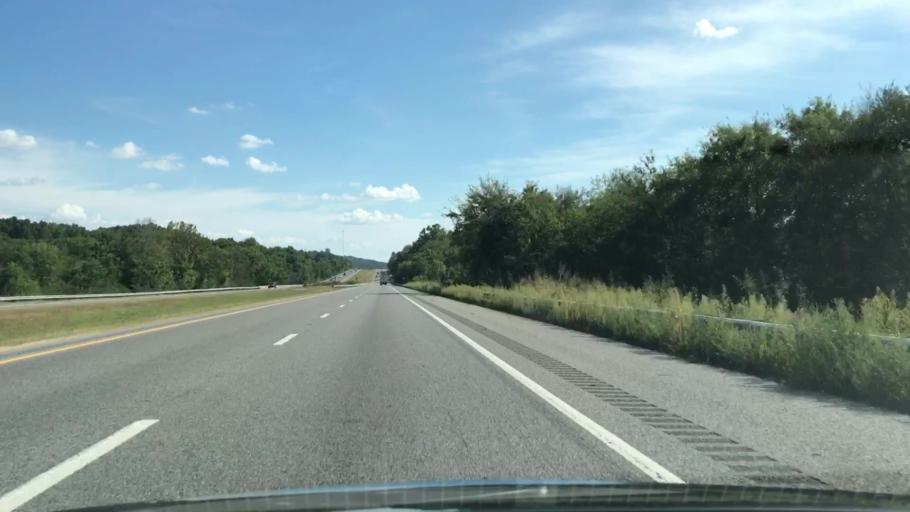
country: US
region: Alabama
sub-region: Limestone County
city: Ardmore
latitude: 35.0531
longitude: -86.8809
